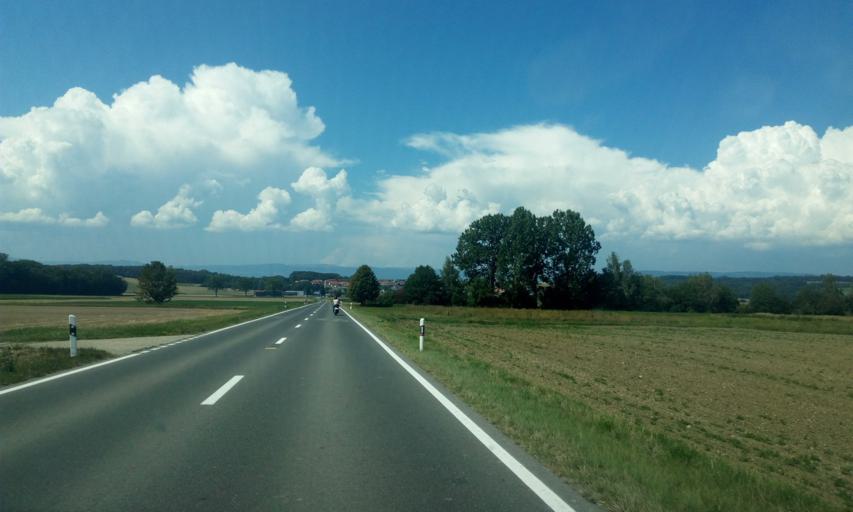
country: CH
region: Fribourg
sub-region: Broye District
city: Domdidier
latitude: 46.8913
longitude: 7.0064
